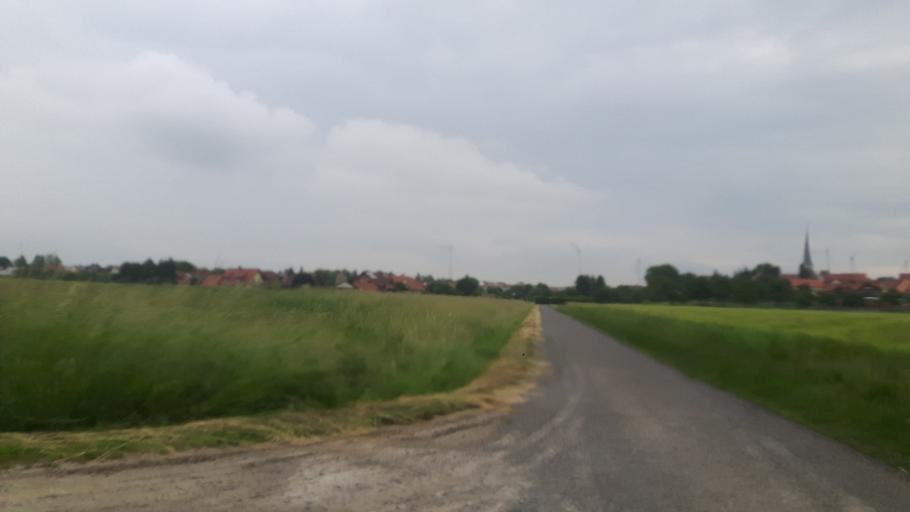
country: DE
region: Bavaria
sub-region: Regierungsbezirk Unterfranken
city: Prosselsheim
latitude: 49.8958
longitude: 10.1178
